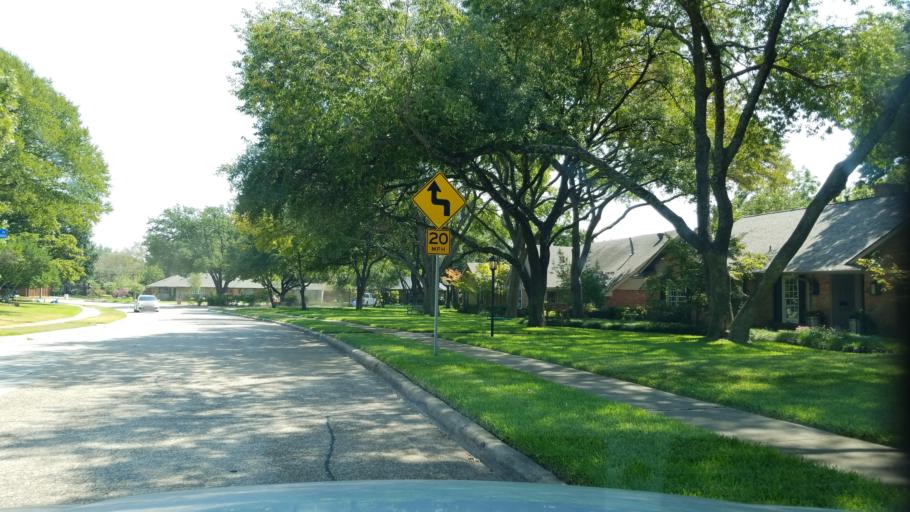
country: US
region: Texas
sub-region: Dallas County
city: Richardson
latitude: 32.9592
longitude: -96.7533
